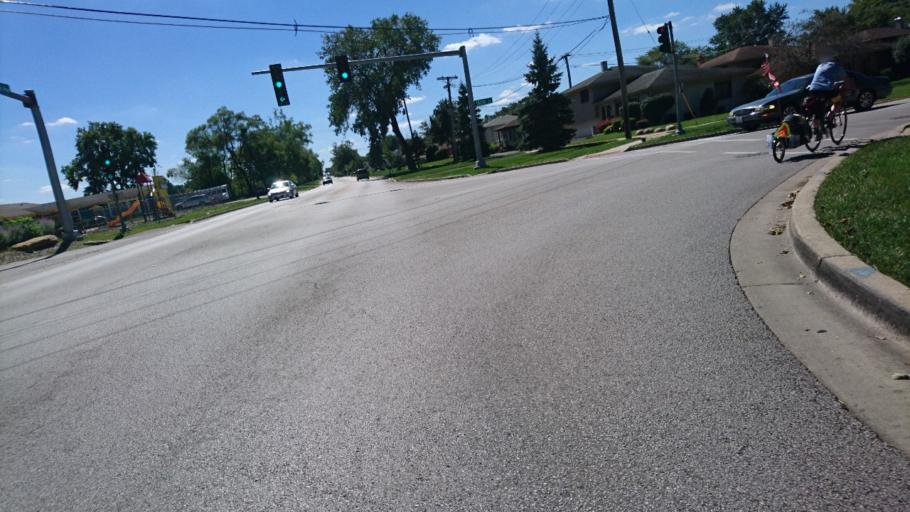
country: US
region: Illinois
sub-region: Cook County
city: Lansing
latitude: 41.5577
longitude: -87.5297
